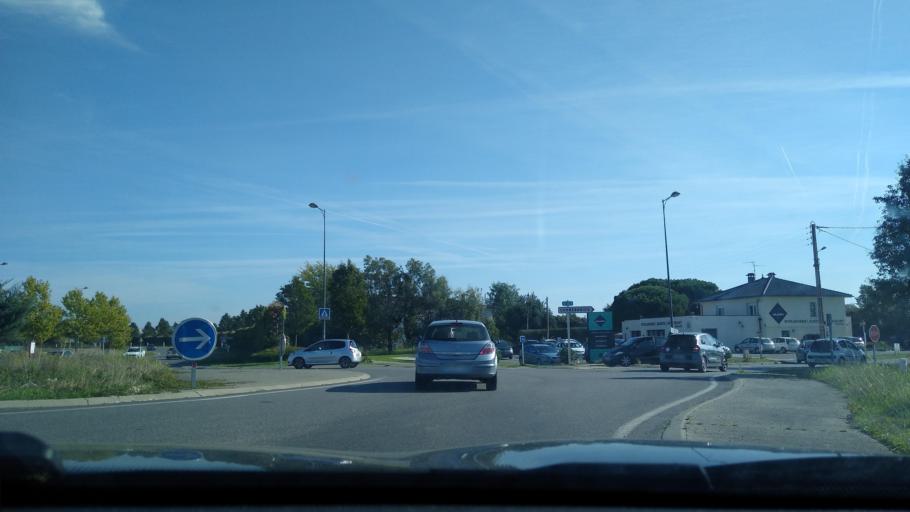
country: FR
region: Midi-Pyrenees
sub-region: Departement de la Haute-Garonne
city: Cornebarrieu
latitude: 43.6588
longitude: 1.3350
